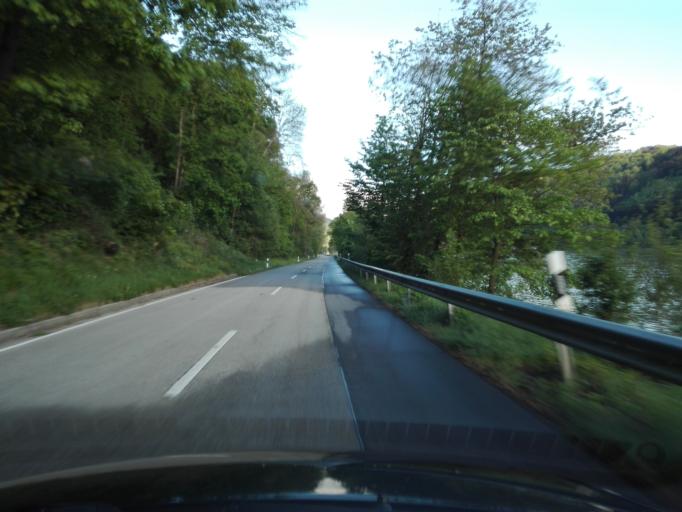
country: DE
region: Bavaria
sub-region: Lower Bavaria
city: Untergriesbach
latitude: 48.5249
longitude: 13.6969
